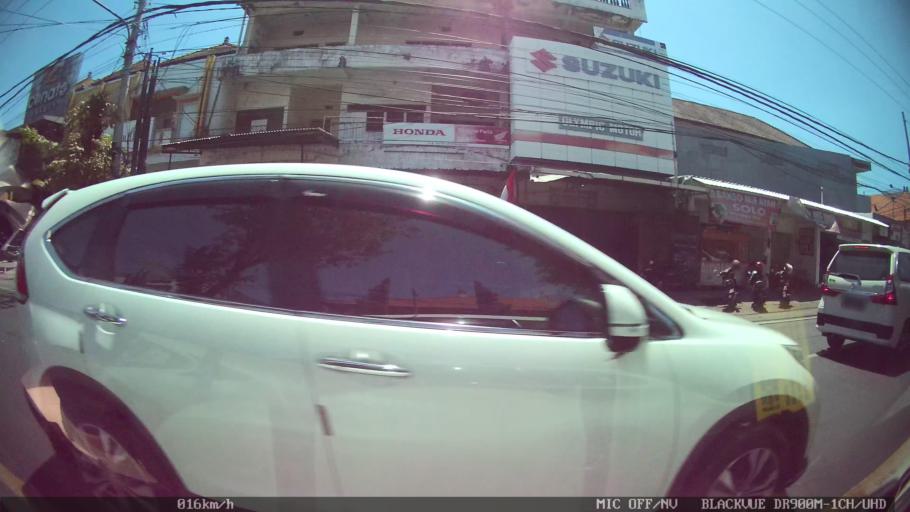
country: ID
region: Bali
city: Banjar Kaliuntu Satu
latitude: -8.1123
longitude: 115.0845
